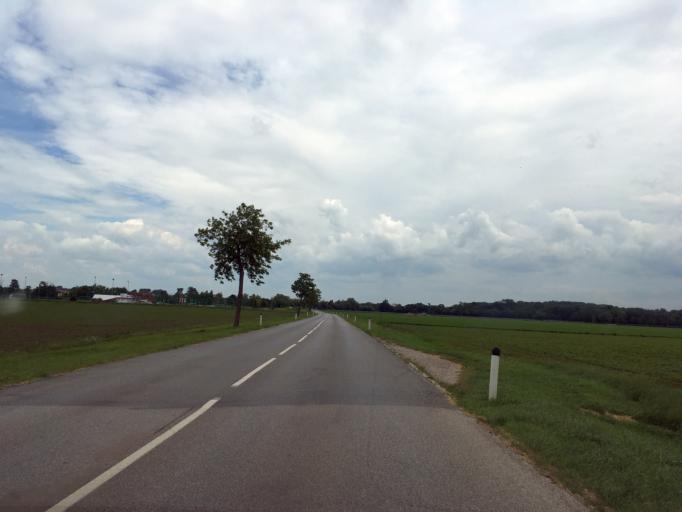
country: AT
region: Lower Austria
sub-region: Politischer Bezirk Modling
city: Laxenburg
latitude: 48.0569
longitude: 16.3452
